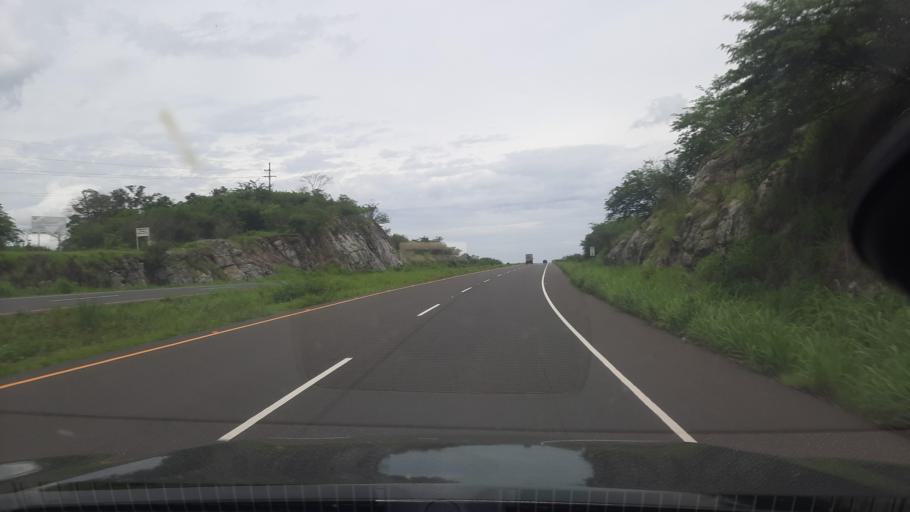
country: HN
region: Valle
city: Aramecina
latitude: 13.7753
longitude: -87.6998
